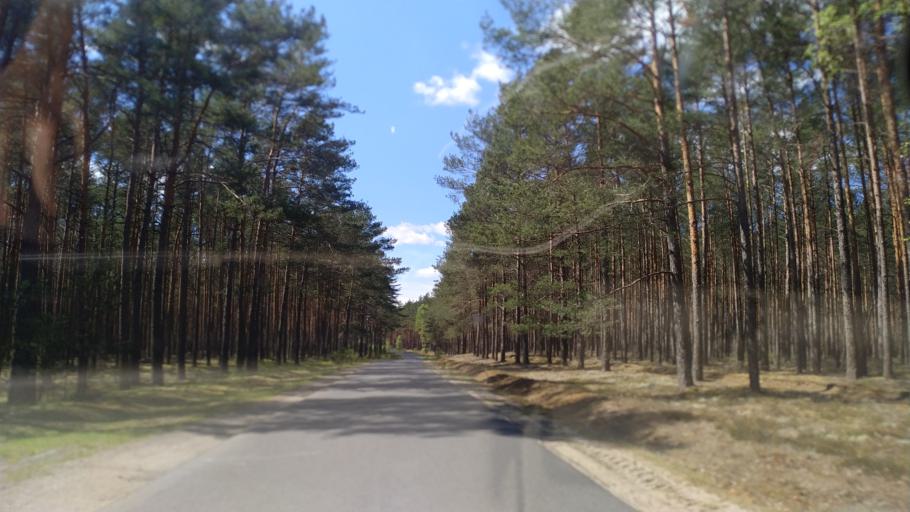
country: PL
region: Greater Poland Voivodeship
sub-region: Powiat zlotowski
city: Tarnowka
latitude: 53.2741
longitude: 16.8261
